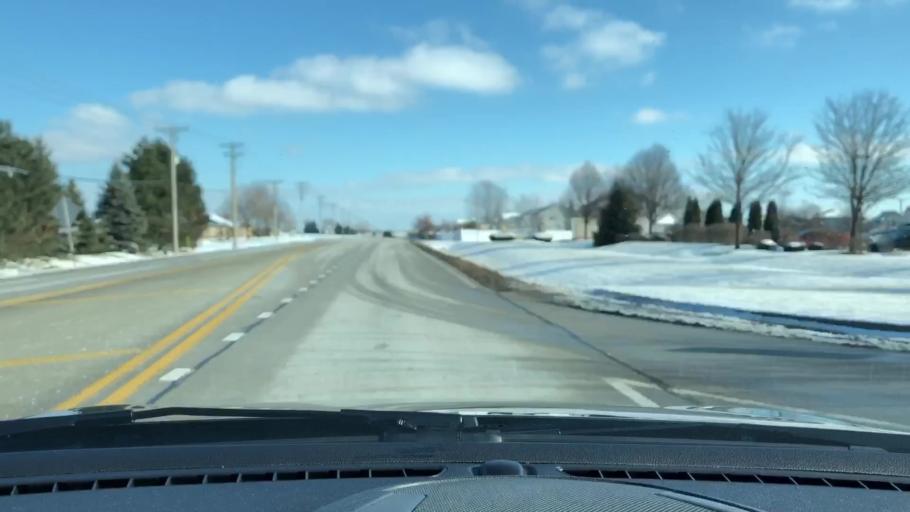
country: US
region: Illinois
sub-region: Will County
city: New Lenox
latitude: 41.4828
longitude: -87.9815
